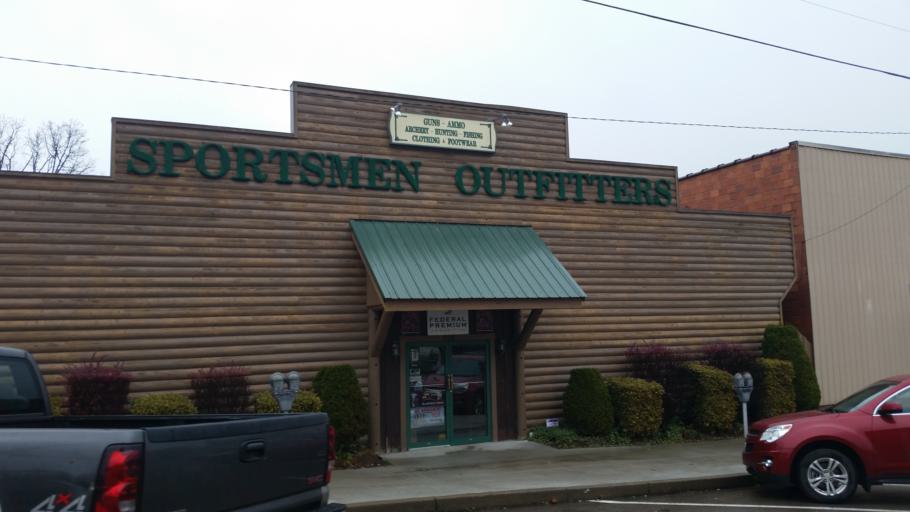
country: US
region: Pennsylvania
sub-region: Clarion County
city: Knox
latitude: 41.2350
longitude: -79.5373
